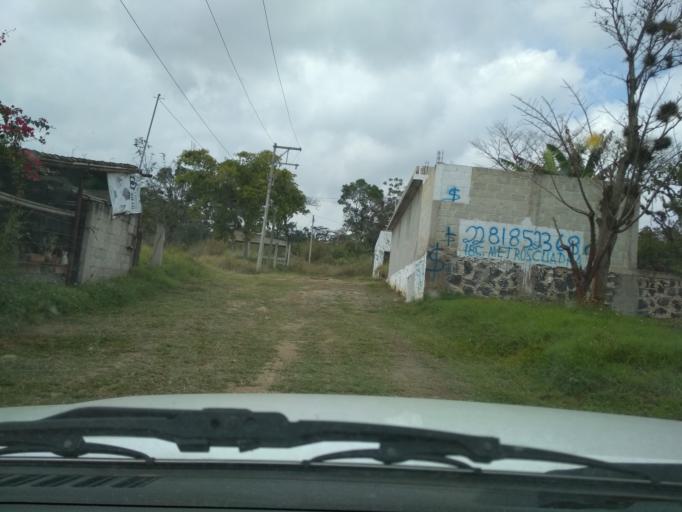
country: MX
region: Veracruz
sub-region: Coatepec
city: Bella Esperanza
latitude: 19.4552
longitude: -96.8628
